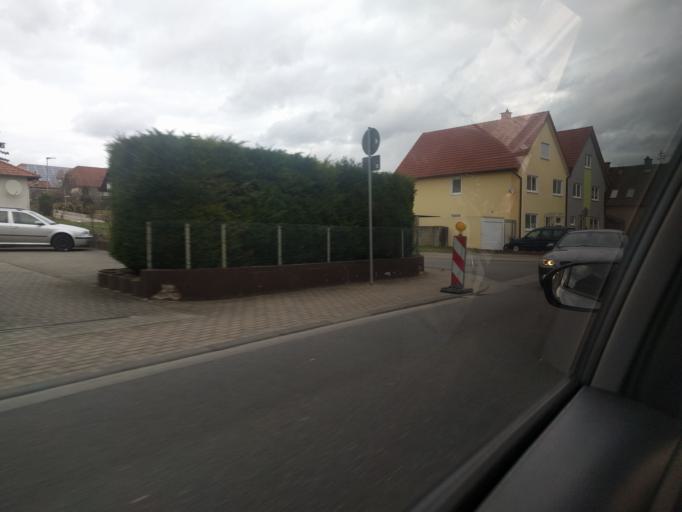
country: DE
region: Rheinland-Pfalz
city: Herxheimweyher
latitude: 49.1518
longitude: 8.2513
